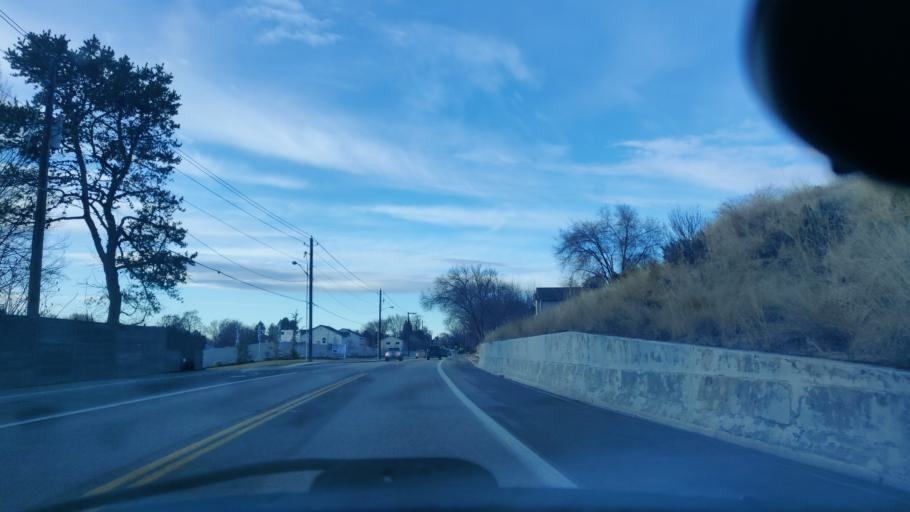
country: US
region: Idaho
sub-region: Ada County
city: Garden City
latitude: 43.6519
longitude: -116.2279
